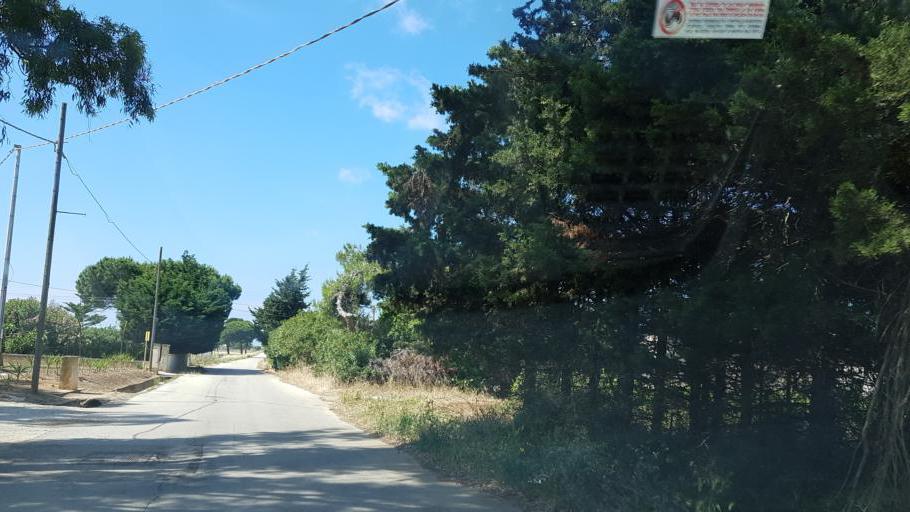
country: IT
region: Apulia
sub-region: Provincia di Brindisi
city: Brindisi
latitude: 40.6527
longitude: 17.8538
